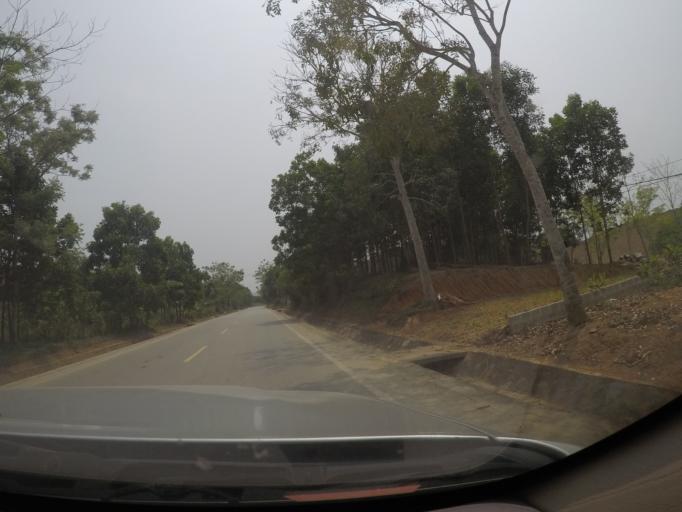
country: VN
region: Thanh Hoa
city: Thi Tran Yen Cat
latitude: 19.7025
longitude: 105.4515
